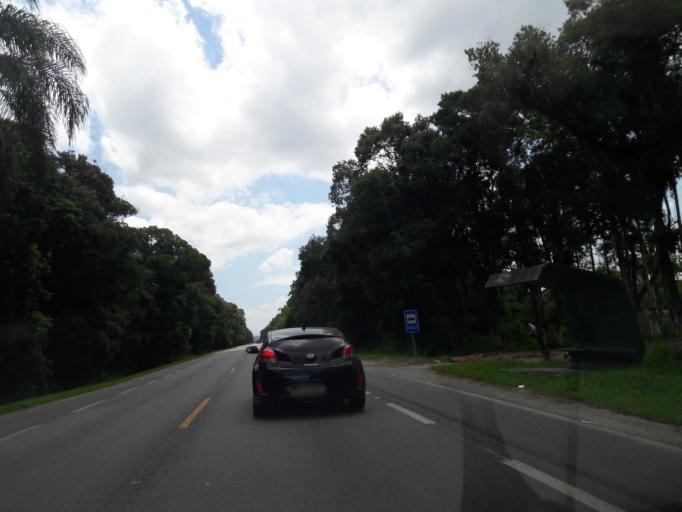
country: BR
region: Parana
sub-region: Pontal Do Parana
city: Pontal do Parana
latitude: -25.6088
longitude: -48.5530
